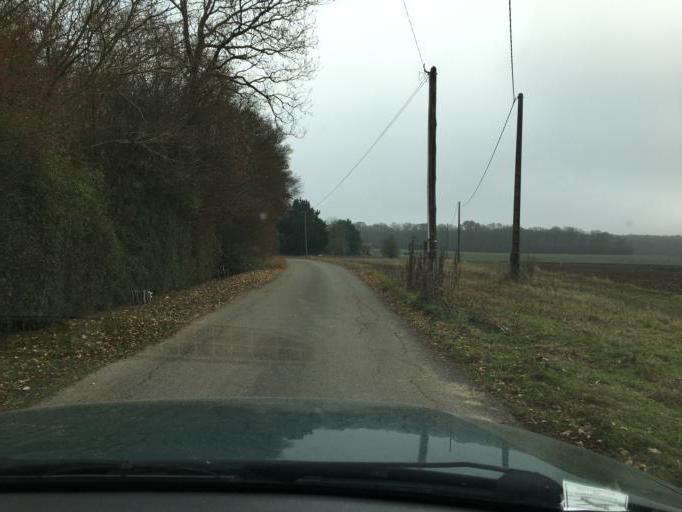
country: FR
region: Centre
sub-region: Departement du Loiret
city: Gidy
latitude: 47.9756
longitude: 1.8448
